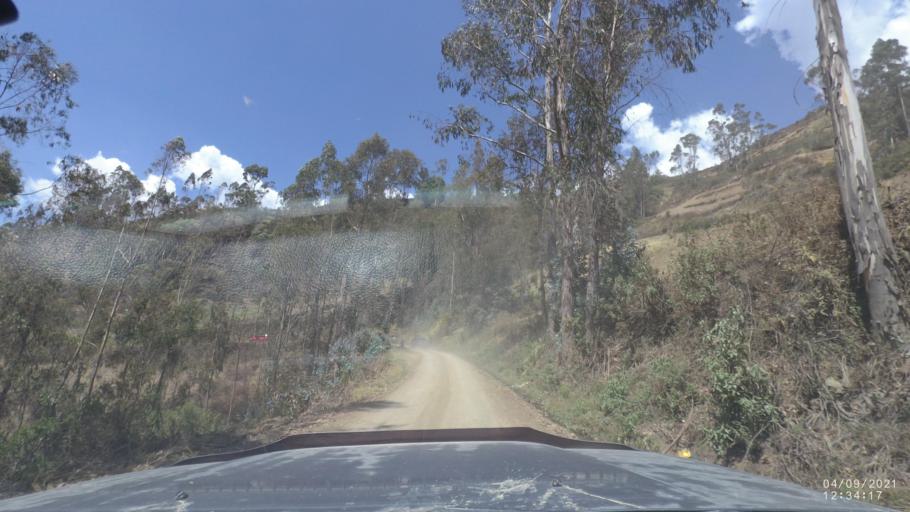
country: BO
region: Cochabamba
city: Colchani
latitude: -17.2224
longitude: -66.5139
